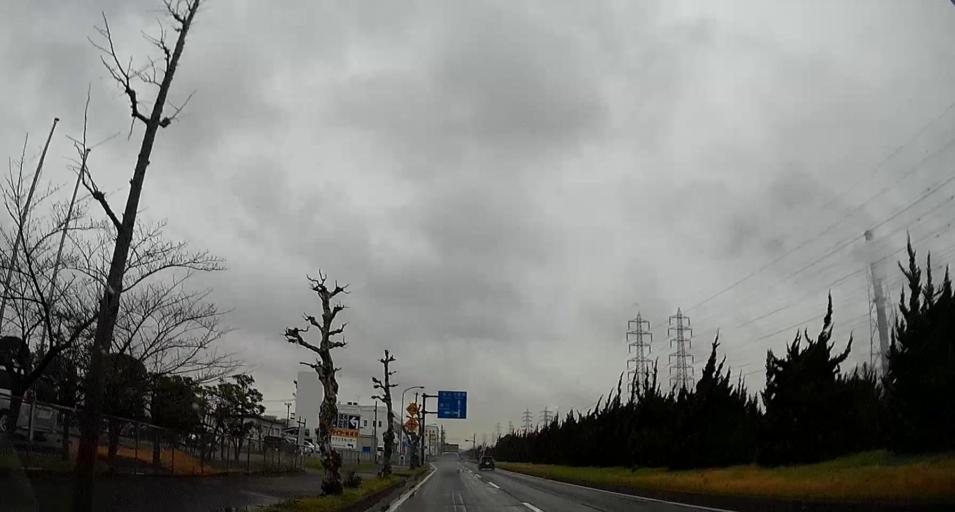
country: JP
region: Chiba
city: Ichihara
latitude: 35.4855
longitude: 140.0395
